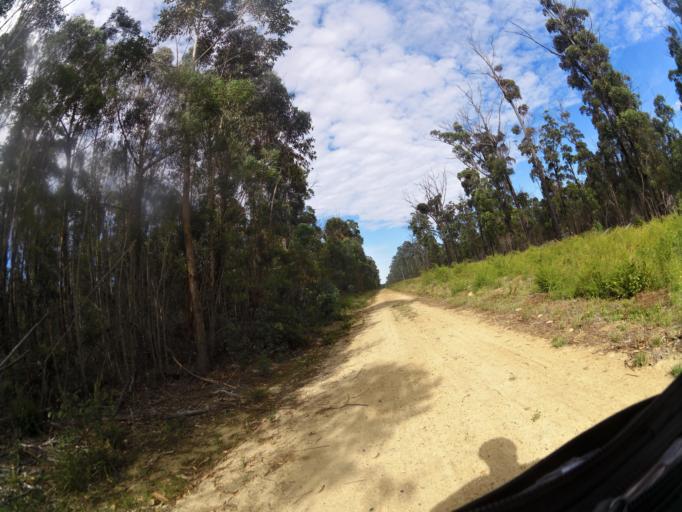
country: AU
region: Victoria
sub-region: East Gippsland
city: Lakes Entrance
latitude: -37.7455
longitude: 148.2415
